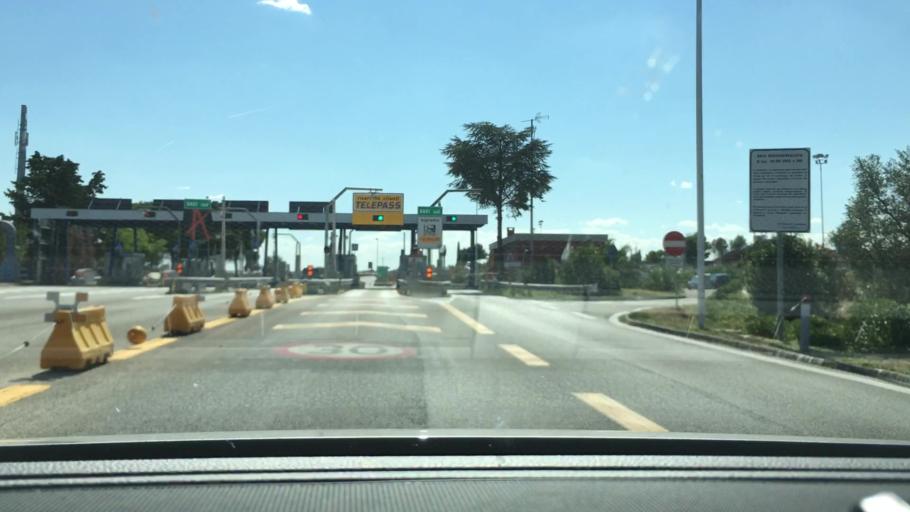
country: IT
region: Apulia
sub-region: Provincia di Bari
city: Bitritto
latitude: 41.0690
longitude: 16.8312
